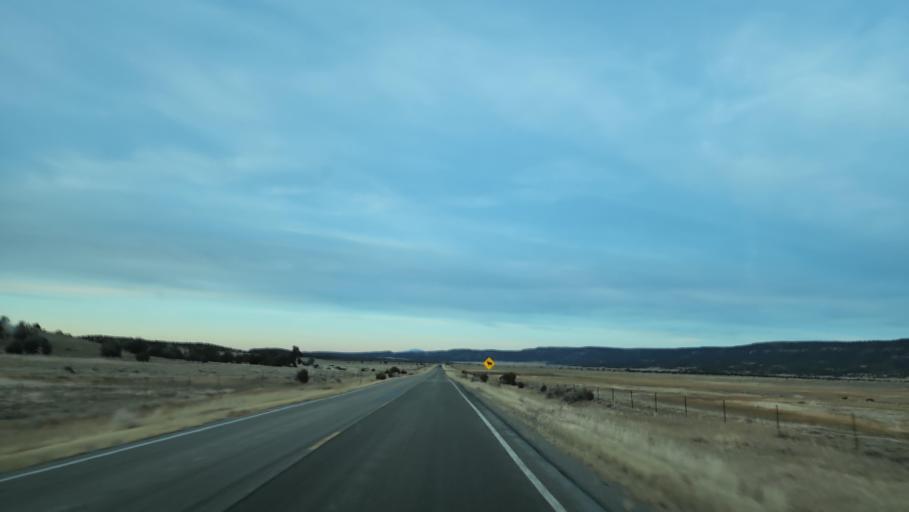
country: US
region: New Mexico
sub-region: Cibola County
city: Grants
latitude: 34.7619
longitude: -107.9555
